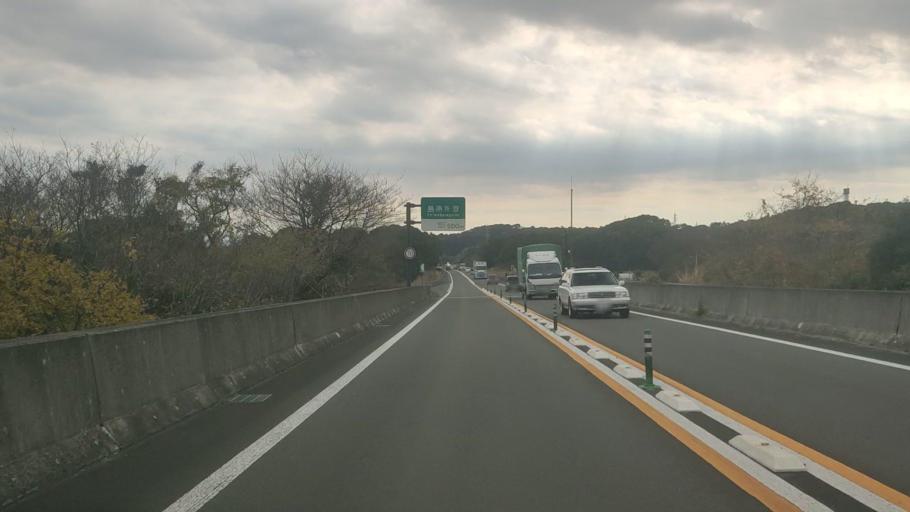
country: JP
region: Nagasaki
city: Shimabara
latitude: 32.7680
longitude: 130.3591
